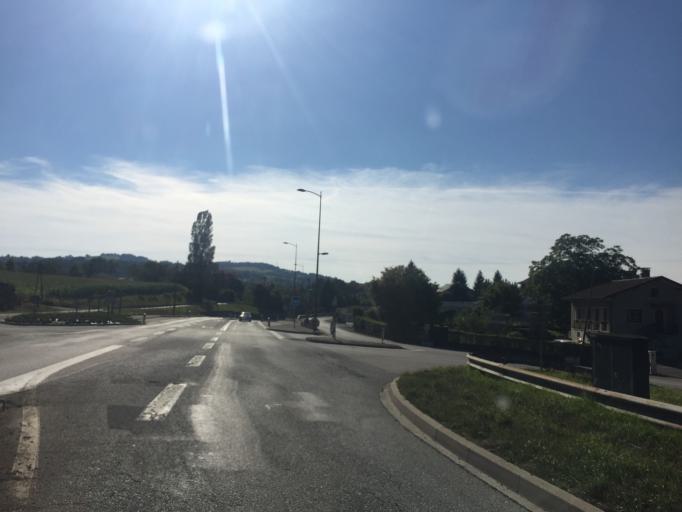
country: FR
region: Rhone-Alpes
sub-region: Departement de la Haute-Savoie
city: Alby-sur-Cheran
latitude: 45.8208
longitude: 6.0343
